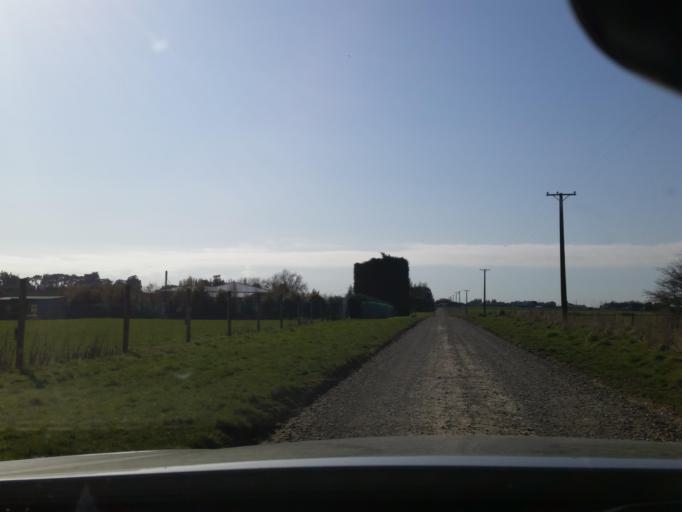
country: NZ
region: Southland
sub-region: Southland District
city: Winton
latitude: -46.2726
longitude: 168.3214
